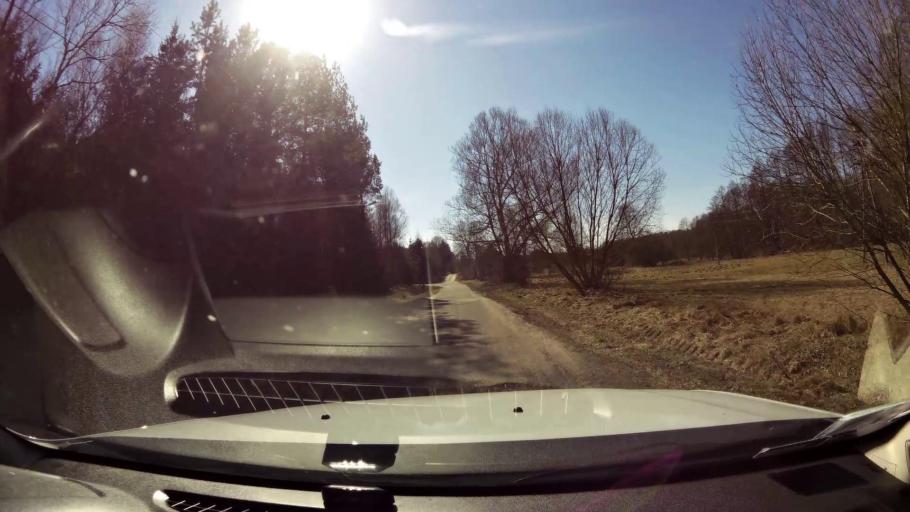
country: PL
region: West Pomeranian Voivodeship
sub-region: Powiat gryfinski
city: Banie
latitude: 53.0359
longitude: 14.6314
